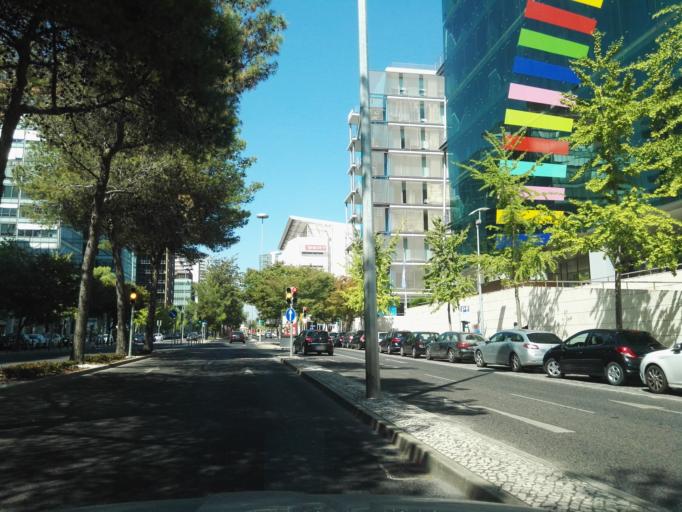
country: PT
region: Lisbon
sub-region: Loures
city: Moscavide
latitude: 38.7700
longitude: -9.0976
